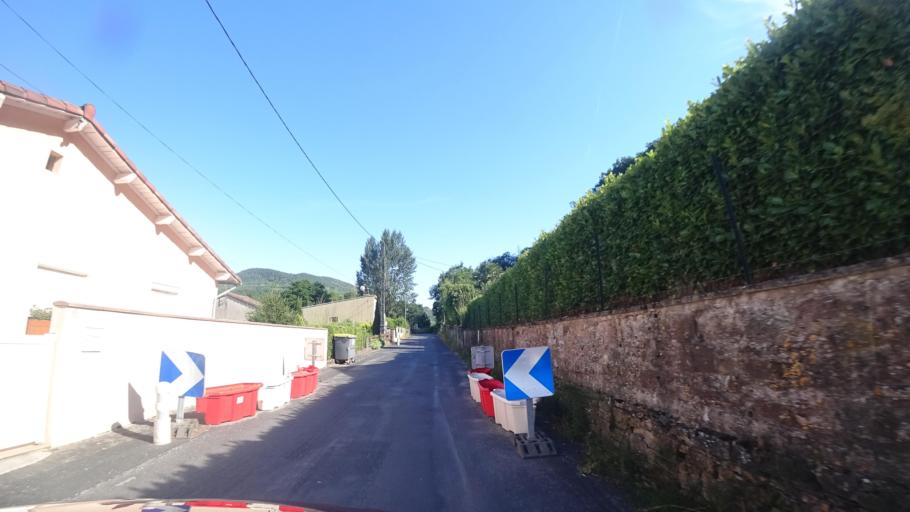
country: FR
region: Midi-Pyrenees
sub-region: Departement de l'Aveyron
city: Saint-Affrique
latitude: 43.9510
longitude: 2.8903
